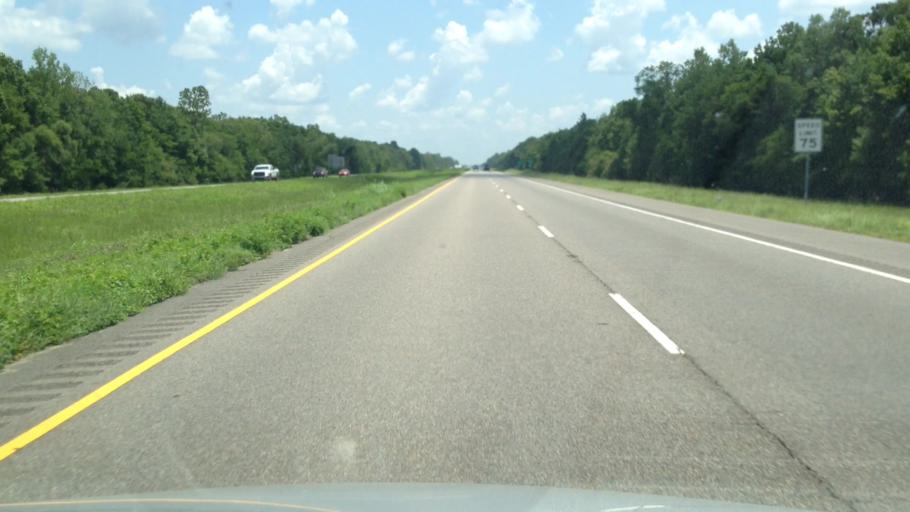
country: US
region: Louisiana
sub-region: Avoyelles Parish
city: Bunkie
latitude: 30.9792
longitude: -92.2990
